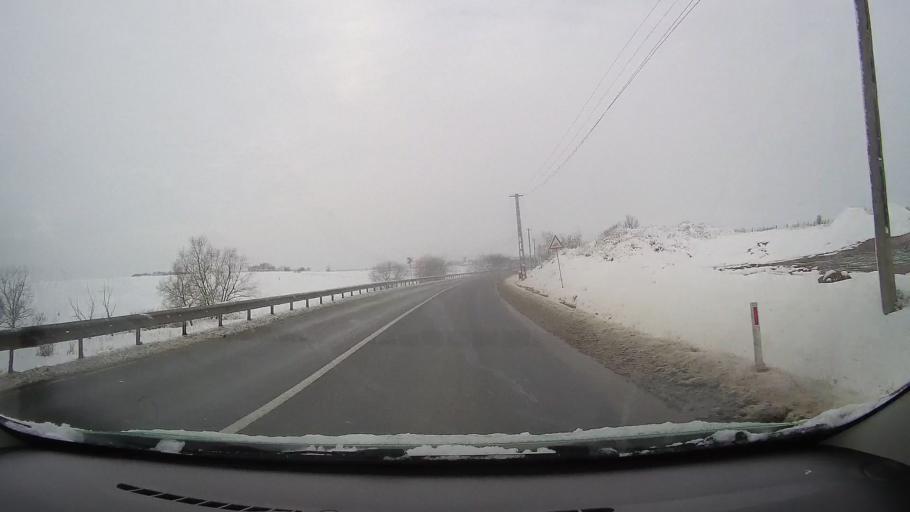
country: RO
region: Alba
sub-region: Municipiul Sebes
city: Lancram
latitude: 45.9835
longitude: 23.5146
